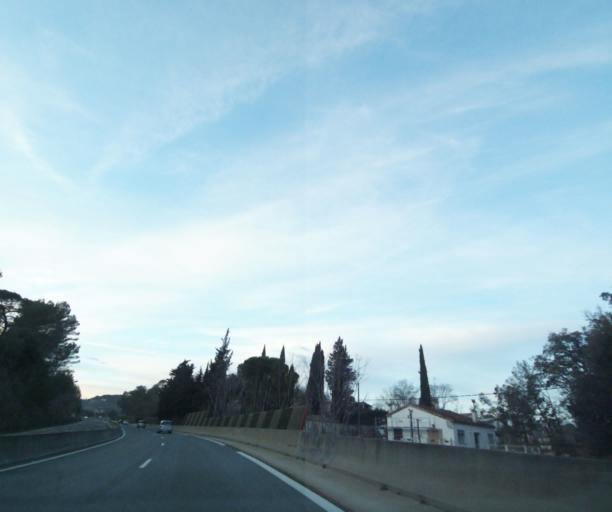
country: FR
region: Provence-Alpes-Cote d'Azur
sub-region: Departement du Var
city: Trans-en-Provence
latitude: 43.4971
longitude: 6.4908
